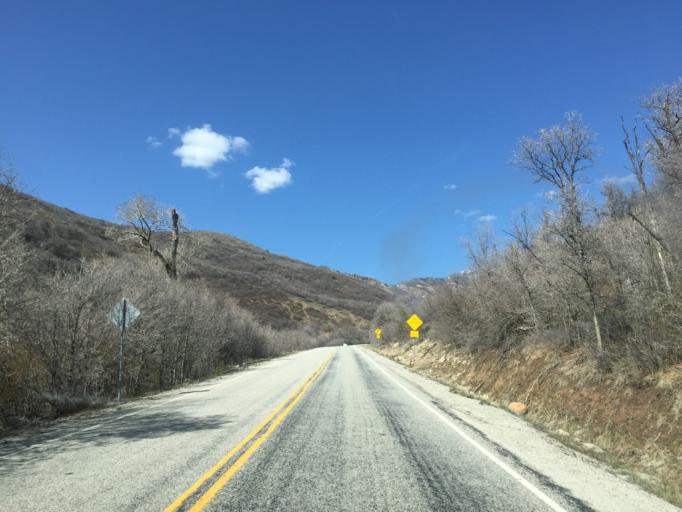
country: US
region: Utah
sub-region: Weber County
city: Wolf Creek
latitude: 41.3453
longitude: -111.8213
